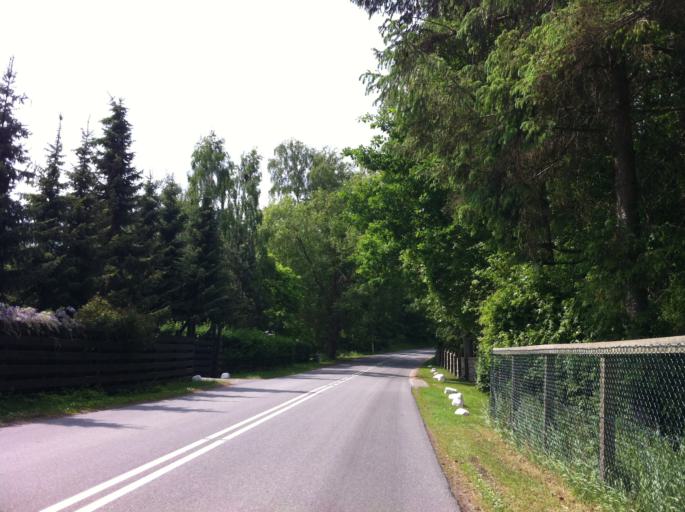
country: DK
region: Capital Region
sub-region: Gribskov Kommune
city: Helsinge
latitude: 56.1117
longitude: 12.2024
